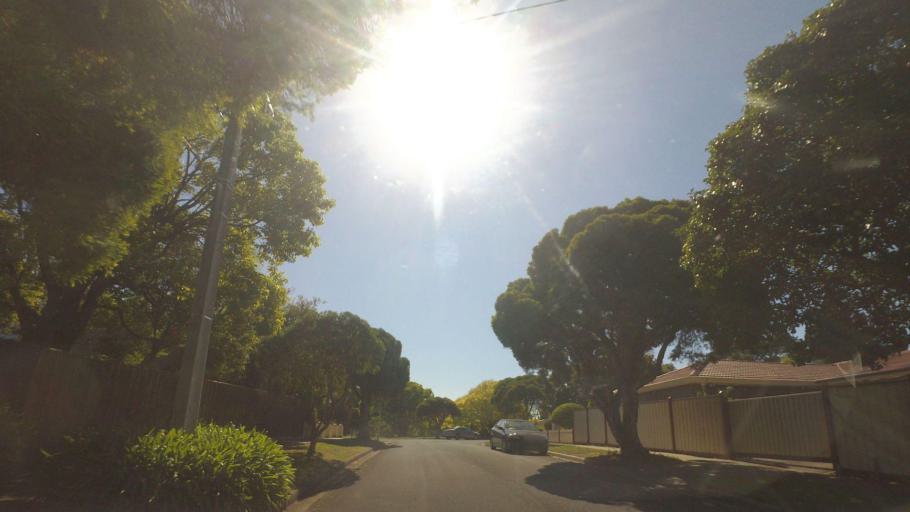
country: AU
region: Victoria
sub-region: Manningham
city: Donvale
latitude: -37.7789
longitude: 145.1708
